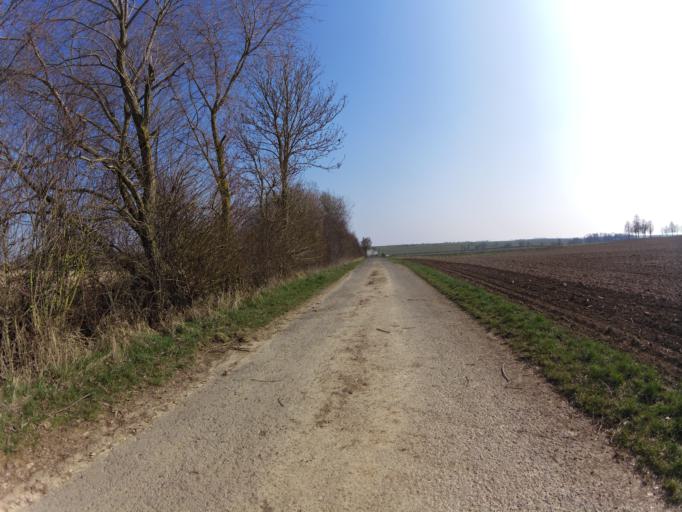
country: DE
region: Bavaria
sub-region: Regierungsbezirk Unterfranken
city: Sulzdorf
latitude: 49.6570
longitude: 9.9148
